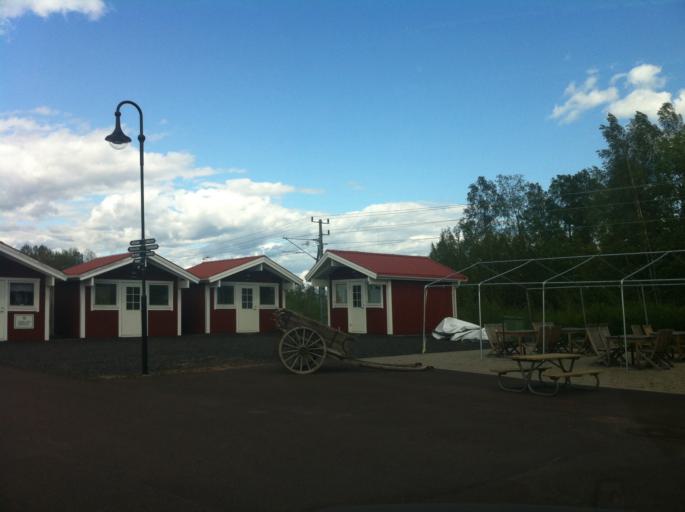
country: SE
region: Vaermland
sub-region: Storfors Kommun
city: Storfors
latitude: 59.4350
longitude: 14.2311
